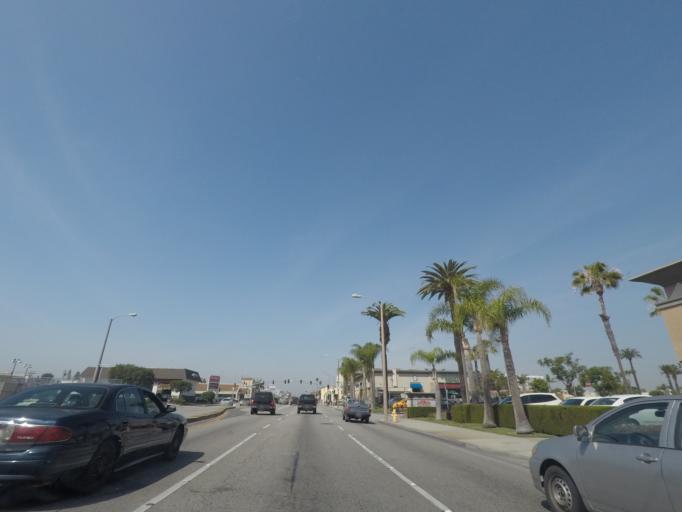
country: US
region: California
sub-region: Los Angeles County
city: Hawthorne
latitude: 33.9165
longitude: -118.3511
